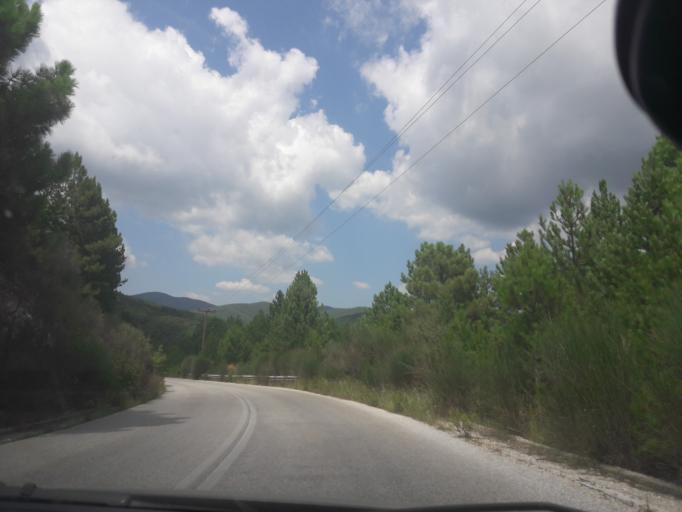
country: GR
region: Central Macedonia
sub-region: Nomos Chalkidikis
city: Polygyros
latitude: 40.3645
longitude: 23.4986
